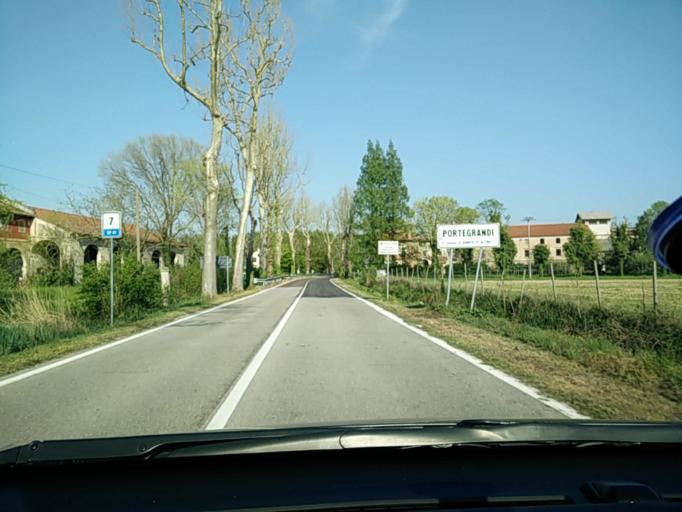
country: IT
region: Veneto
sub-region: Provincia di Venezia
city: Quarto d'Altino
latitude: 45.5609
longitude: 12.4276
